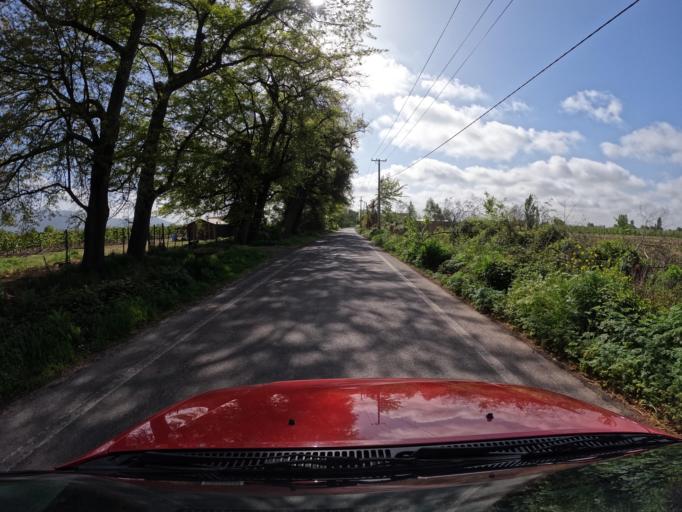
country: CL
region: Maule
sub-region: Provincia de Curico
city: Teno
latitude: -34.8809
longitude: -71.2400
